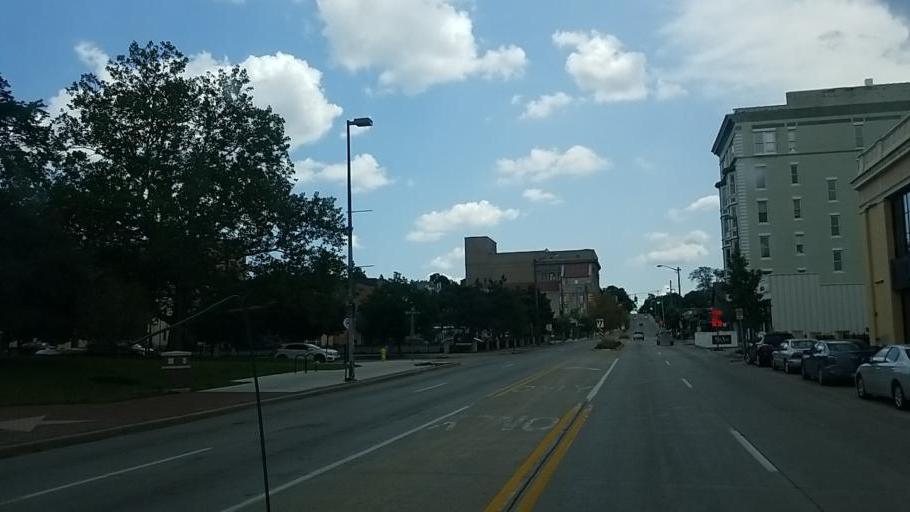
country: US
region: Michigan
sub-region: Kent County
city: Grand Rapids
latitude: 42.9631
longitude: -85.6667
